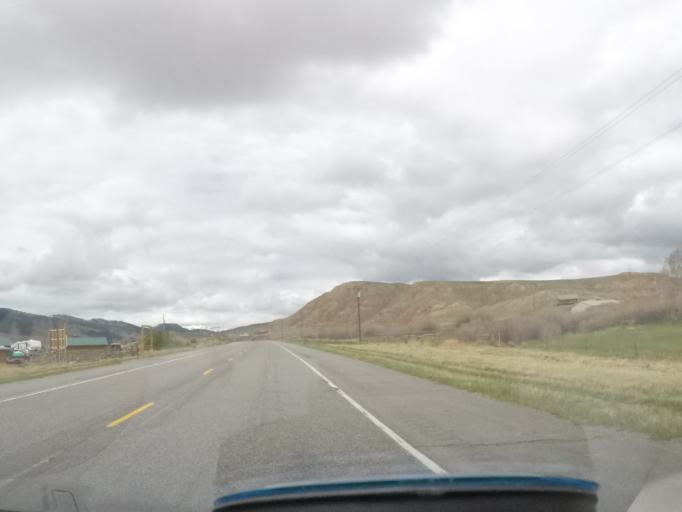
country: US
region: Wyoming
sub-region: Sublette County
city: Pinedale
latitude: 43.5662
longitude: -109.7059
